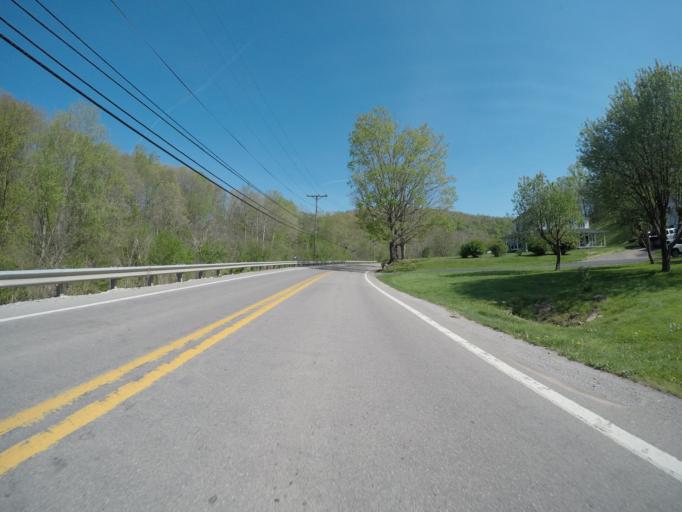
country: US
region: West Virginia
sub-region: Kanawha County
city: Clendenin
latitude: 38.5031
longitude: -81.3499
